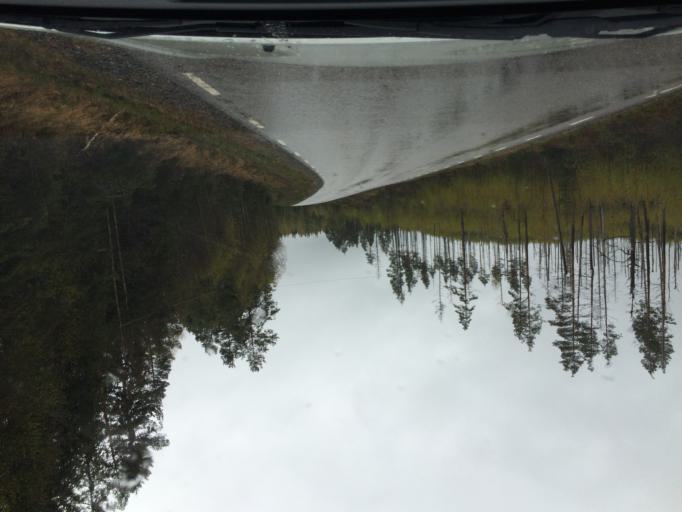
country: SE
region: Dalarna
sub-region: Ludvika Kommun
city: Grangesberg
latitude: 60.0413
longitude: 14.9084
